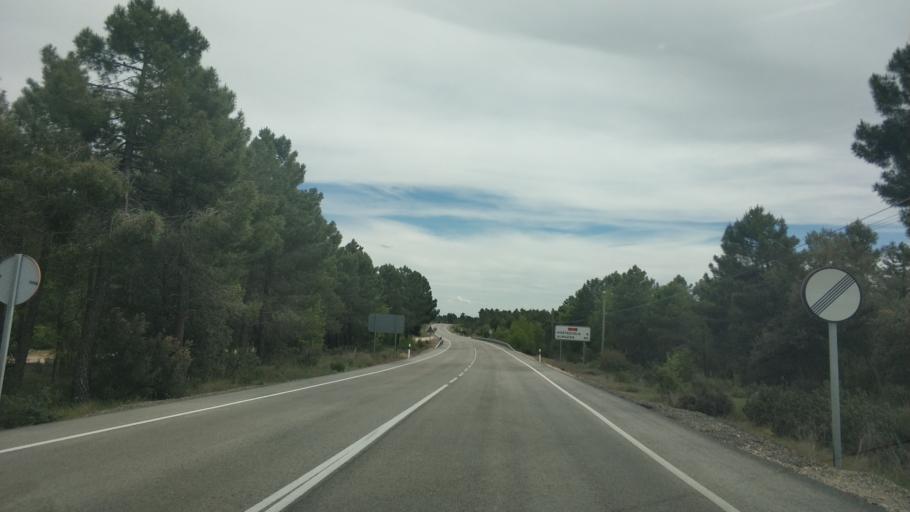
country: ES
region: Castille and Leon
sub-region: Provincia de Soria
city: Valdenebro
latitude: 41.5390
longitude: -2.9537
